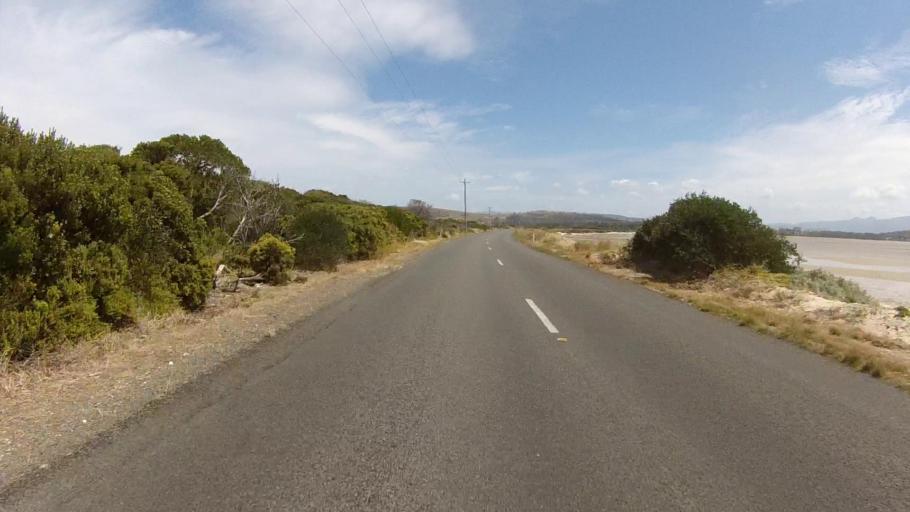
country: AU
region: Tasmania
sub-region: Clarence
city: Sandford
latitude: -43.0324
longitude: 147.4547
